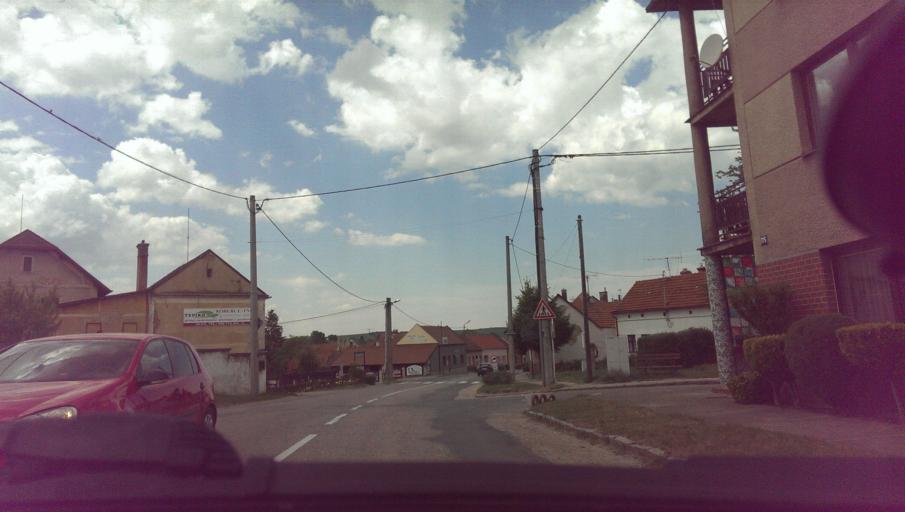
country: CZ
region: Zlin
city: Hluk
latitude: 48.9844
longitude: 17.5366
